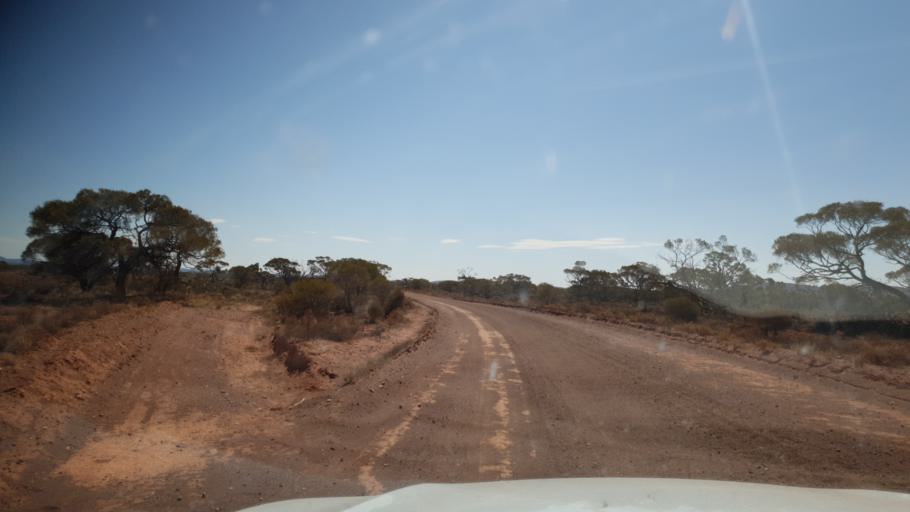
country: AU
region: South Australia
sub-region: Kimba
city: Caralue
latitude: -32.5025
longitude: 136.0975
